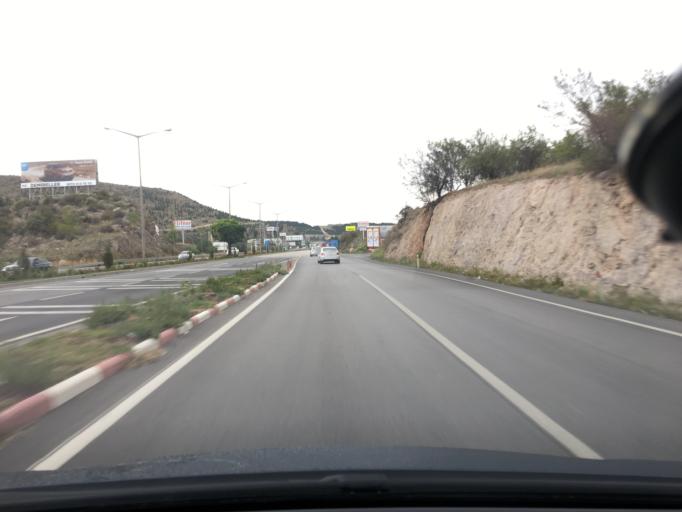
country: TR
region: Afyonkarahisar
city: Afyonkarahisar
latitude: 38.7916
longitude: 30.4531
